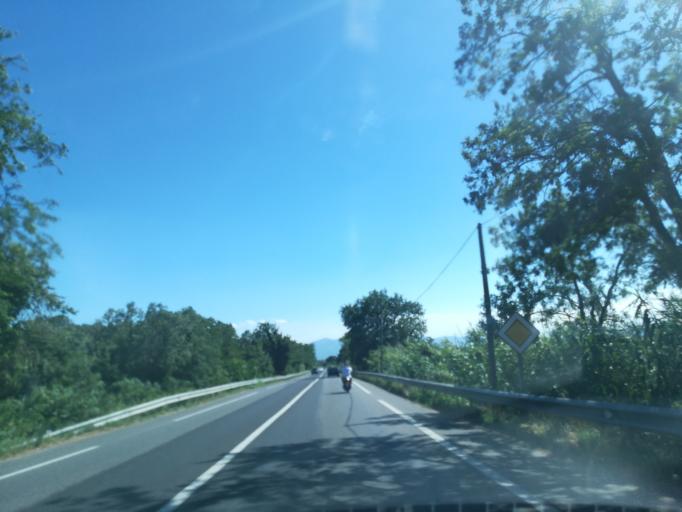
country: FR
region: Languedoc-Roussillon
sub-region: Departement des Pyrenees-Orientales
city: Villemolaque
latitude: 42.6068
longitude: 2.8599
